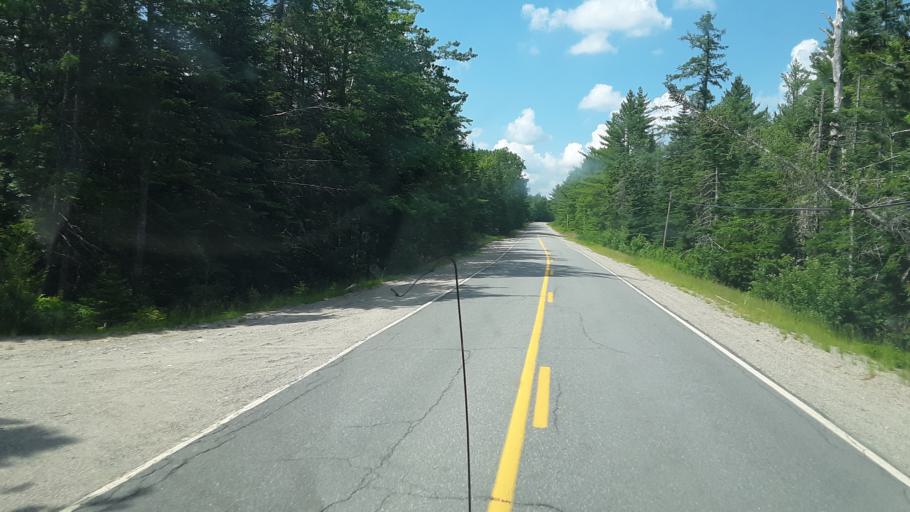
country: US
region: Maine
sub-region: Washington County
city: Machias
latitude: 44.8860
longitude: -67.6221
